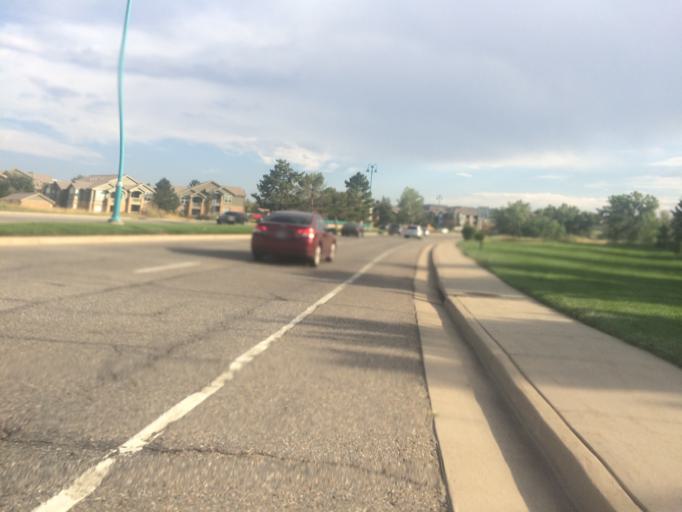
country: US
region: Colorado
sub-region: Boulder County
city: Superior
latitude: 39.9346
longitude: -105.1458
